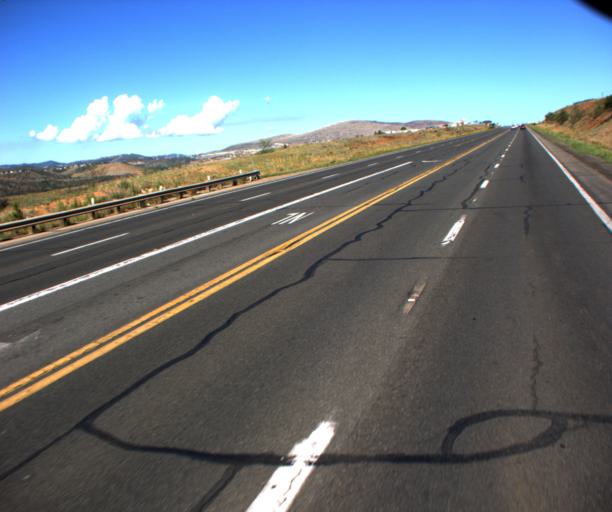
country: US
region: Arizona
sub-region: Yavapai County
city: Prescott Valley
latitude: 34.5808
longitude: -112.3015
